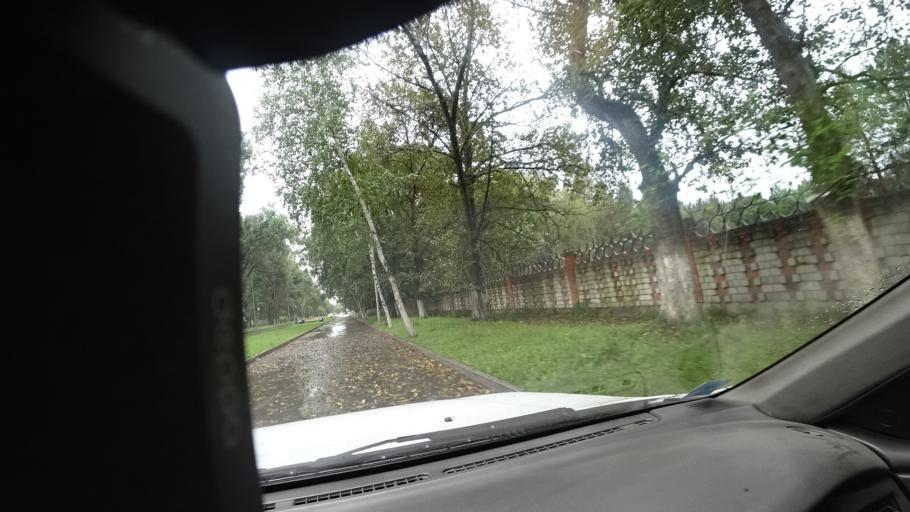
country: RU
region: Primorskiy
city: Dal'nerechensk
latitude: 45.9332
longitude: 133.7258
